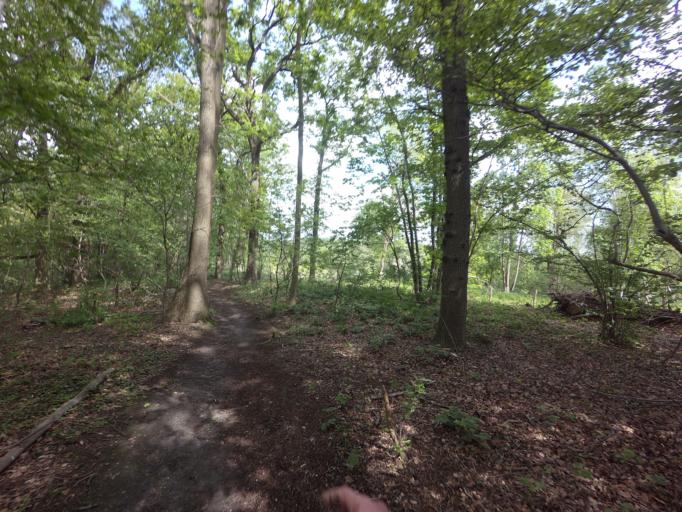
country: NL
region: Limburg
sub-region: Valkenburg aan de Geul
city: Berg
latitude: 50.8358
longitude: 5.7747
